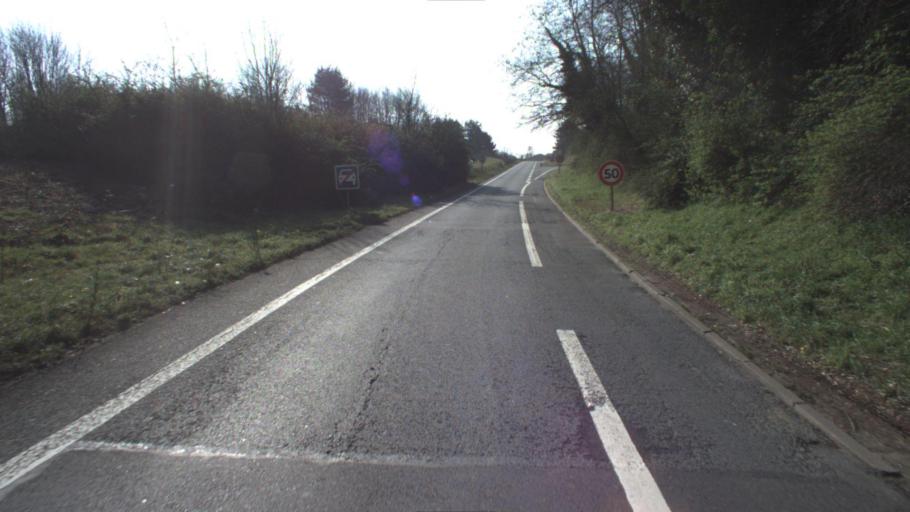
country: FR
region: Ile-de-France
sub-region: Departement de l'Essonne
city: Linas
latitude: 48.6260
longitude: 2.2600
